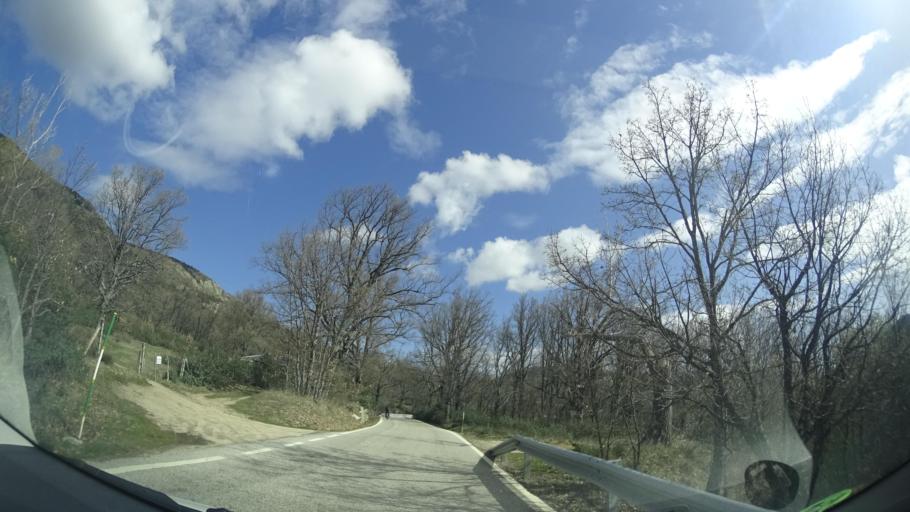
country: ES
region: Madrid
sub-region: Provincia de Madrid
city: Miraflores de la Sierra
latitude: 40.8421
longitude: -3.7665
